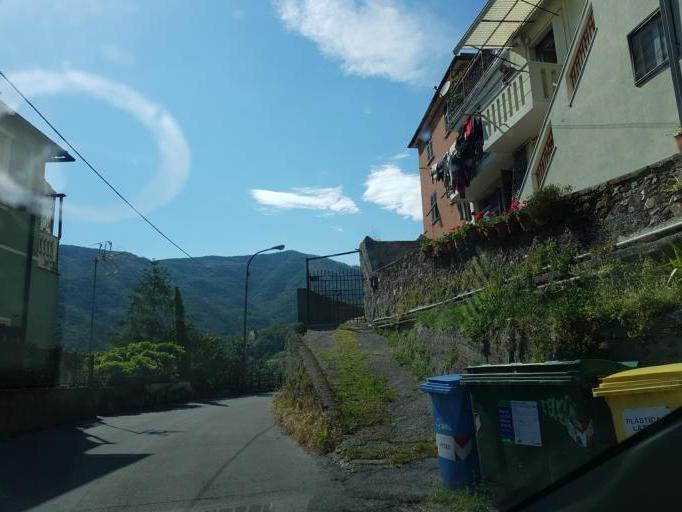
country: IT
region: Liguria
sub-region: Provincia di Genova
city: Genoa
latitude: 44.4568
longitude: 8.8900
